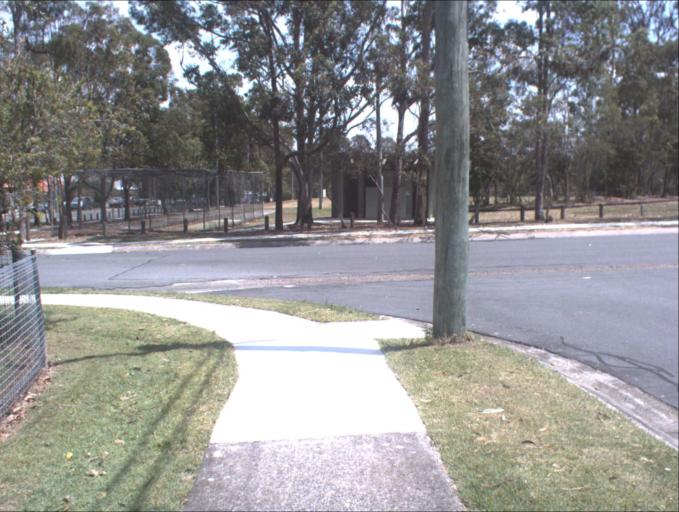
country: AU
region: Queensland
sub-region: Logan
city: Woodridge
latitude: -27.6359
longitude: 153.0983
